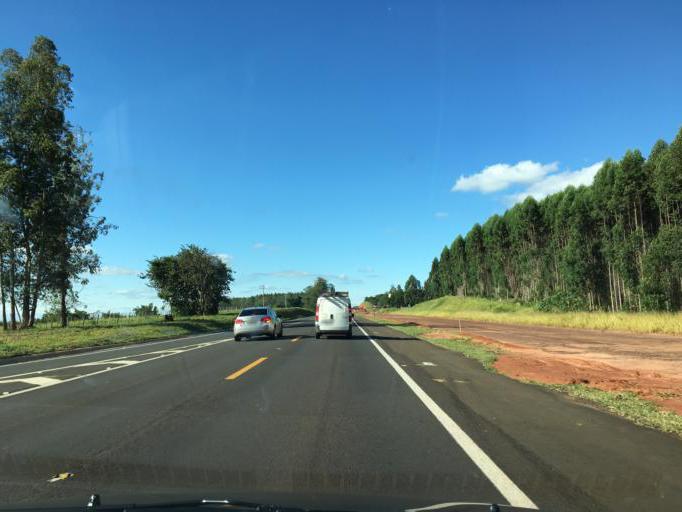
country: BR
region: Sao Paulo
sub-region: Duartina
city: Duartina
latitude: -22.5290
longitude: -49.3307
